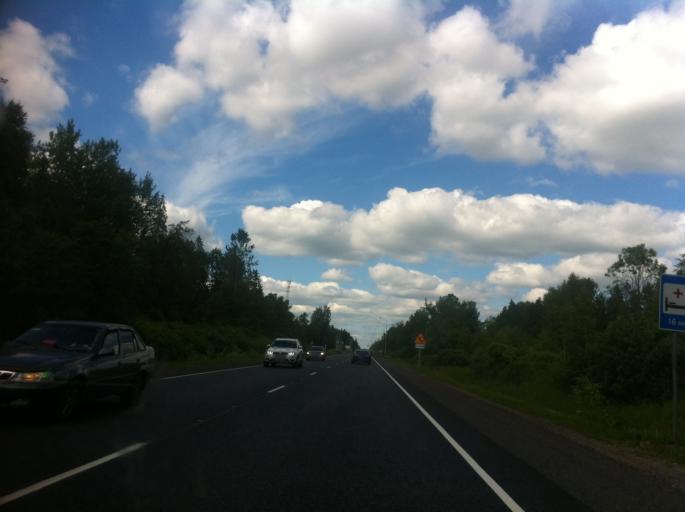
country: RU
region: Leningrad
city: Luga
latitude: 58.7391
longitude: 29.8896
